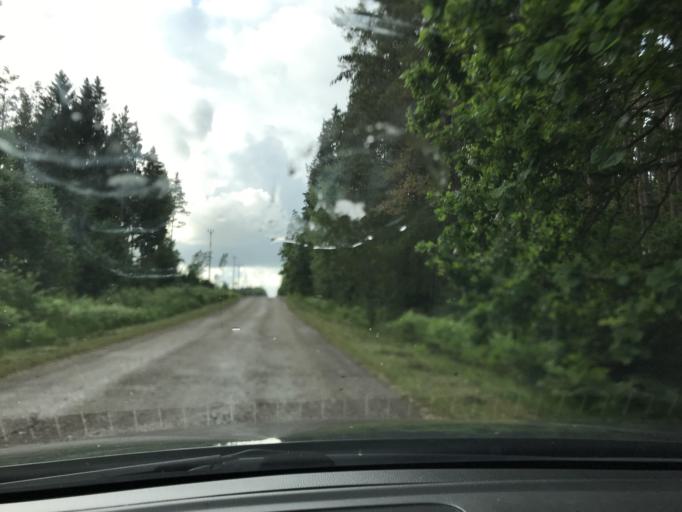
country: LV
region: Alsunga
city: Alsunga
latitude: 56.9869
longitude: 21.6298
